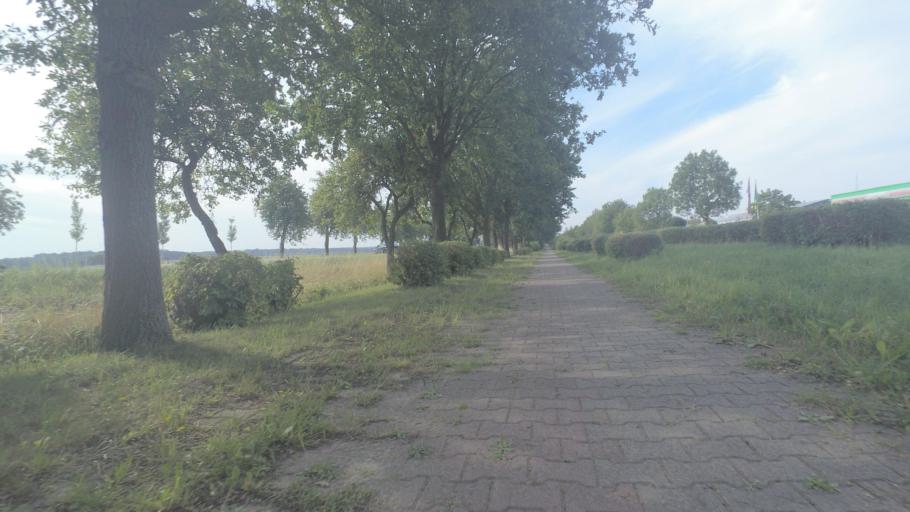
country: DE
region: Mecklenburg-Vorpommern
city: Wackerow
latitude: 53.7189
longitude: 12.9164
